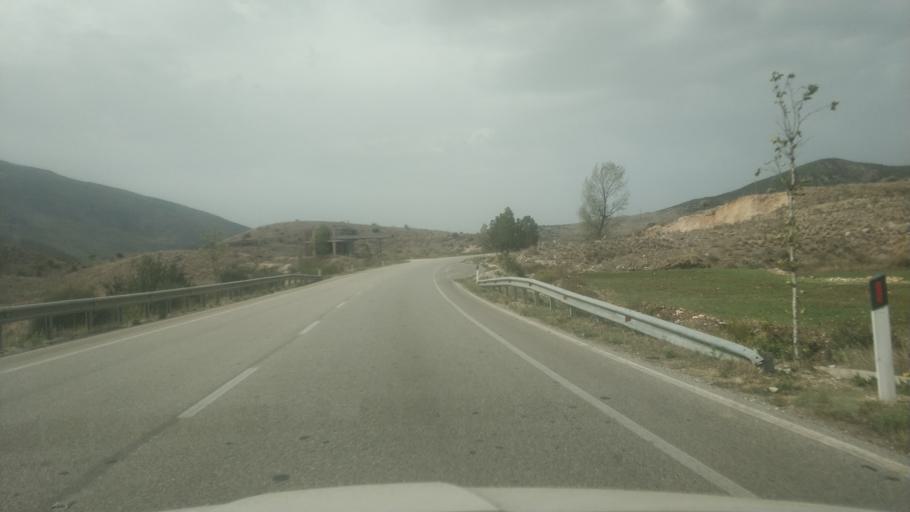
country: AL
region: Gjirokaster
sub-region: Rrethi i Tepelenes
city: Memaliaj
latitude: 40.3562
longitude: 19.9360
